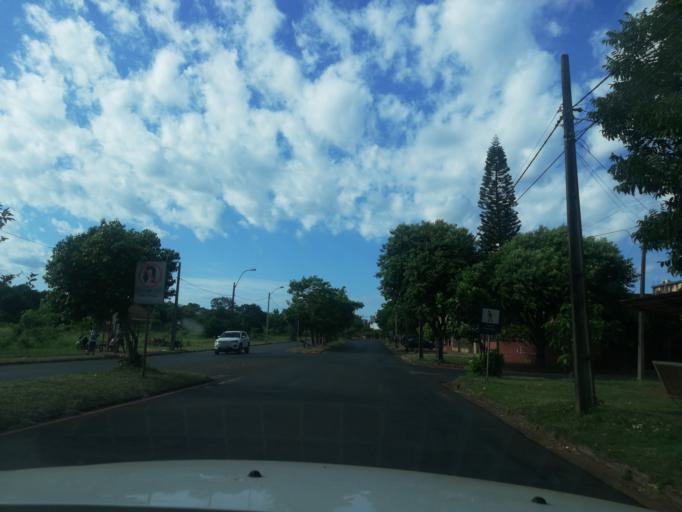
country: PY
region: Itapua
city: Encarnacion
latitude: -27.3513
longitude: -55.8490
